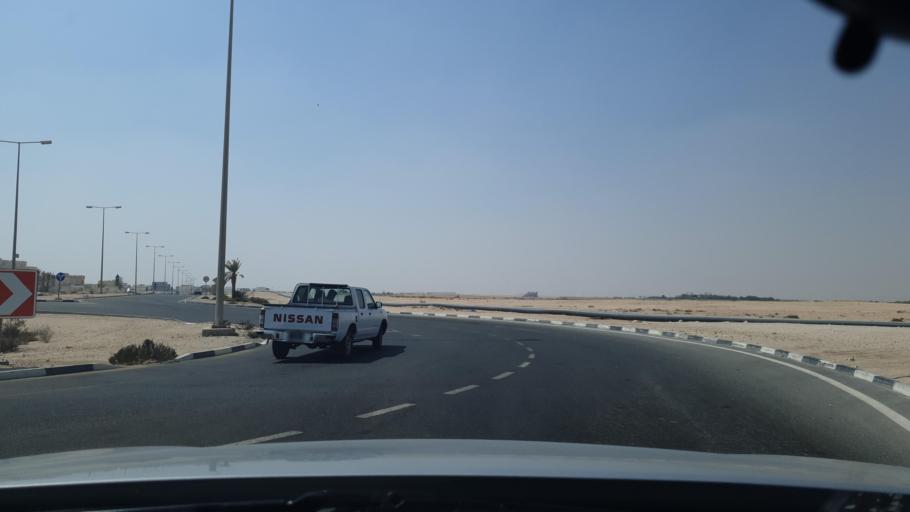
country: QA
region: Al Khawr
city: Al Khawr
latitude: 25.6844
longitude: 51.4810
